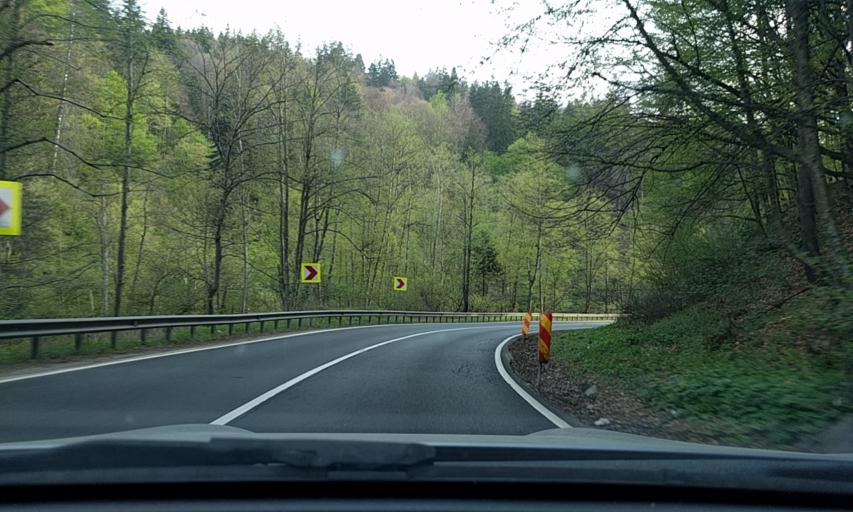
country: RO
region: Covasna
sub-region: Comuna Bretcu
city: Bretcu
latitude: 46.0866
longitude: 26.3999
